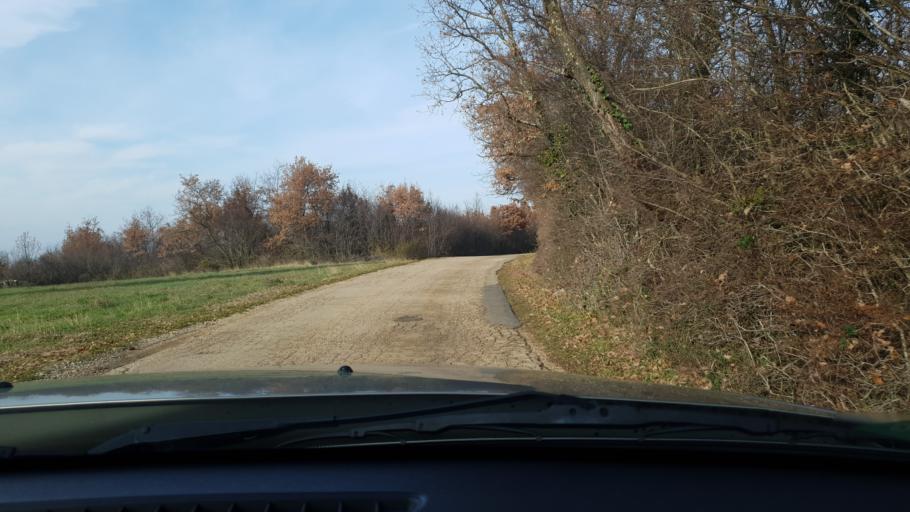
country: HR
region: Istarska
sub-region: Grad Porec
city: Porec
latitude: 45.2544
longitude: 13.6603
